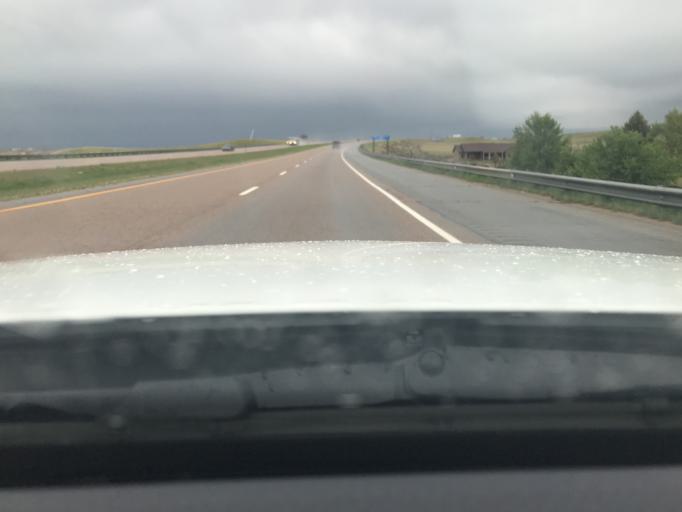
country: US
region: Wyoming
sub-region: Converse County
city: Douglas
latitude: 42.7383
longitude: -105.3593
